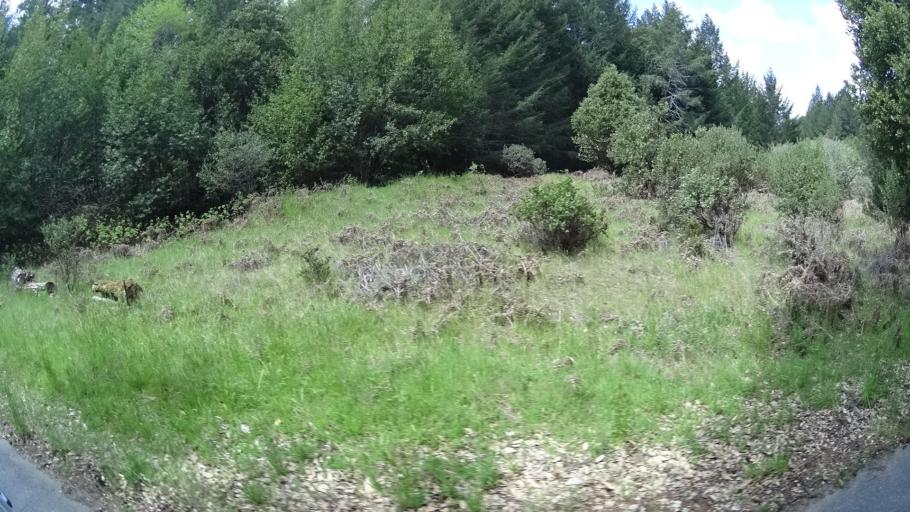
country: US
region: California
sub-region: Humboldt County
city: Redway
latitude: 40.0447
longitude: -123.9581
